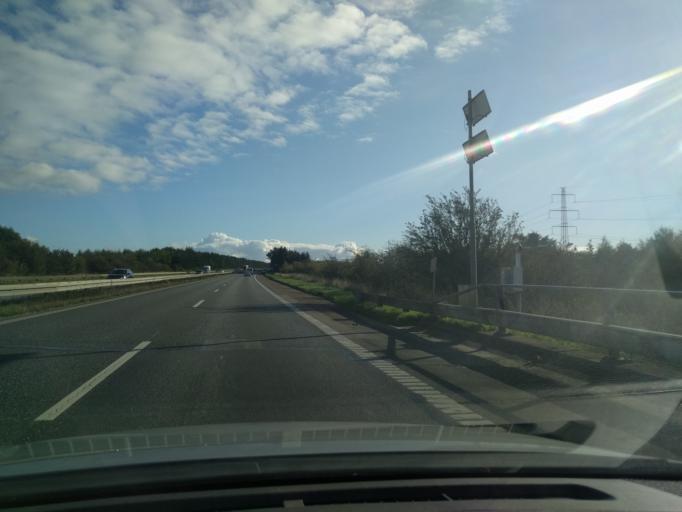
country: DK
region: Zealand
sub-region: Ringsted Kommune
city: Ringsted
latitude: 55.4549
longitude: 11.7596
